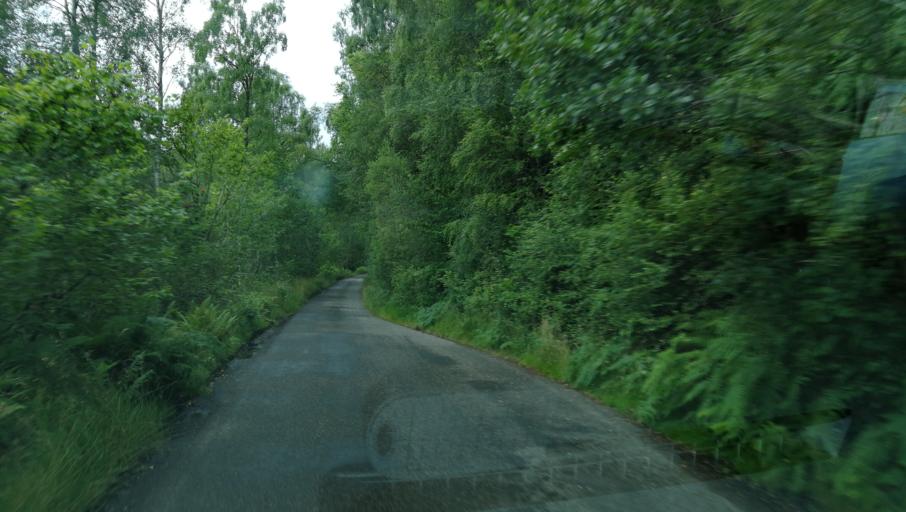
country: GB
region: Scotland
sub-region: Highland
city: Beauly
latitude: 57.3154
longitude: -4.8362
